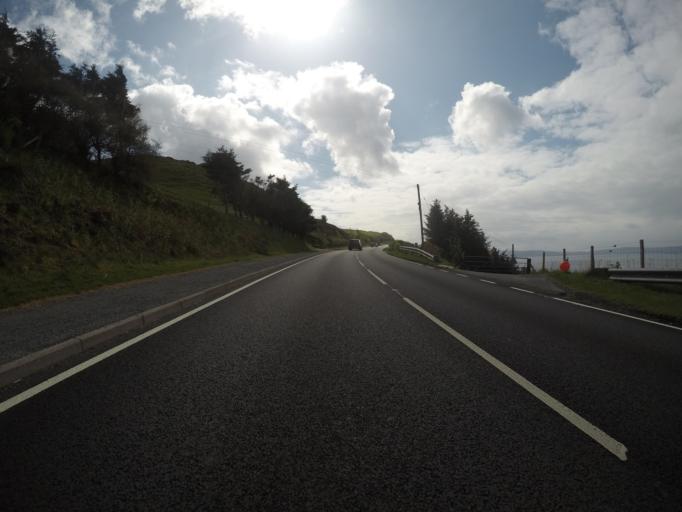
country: GB
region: Scotland
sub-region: Highland
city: Portree
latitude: 57.5833
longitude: -6.3577
